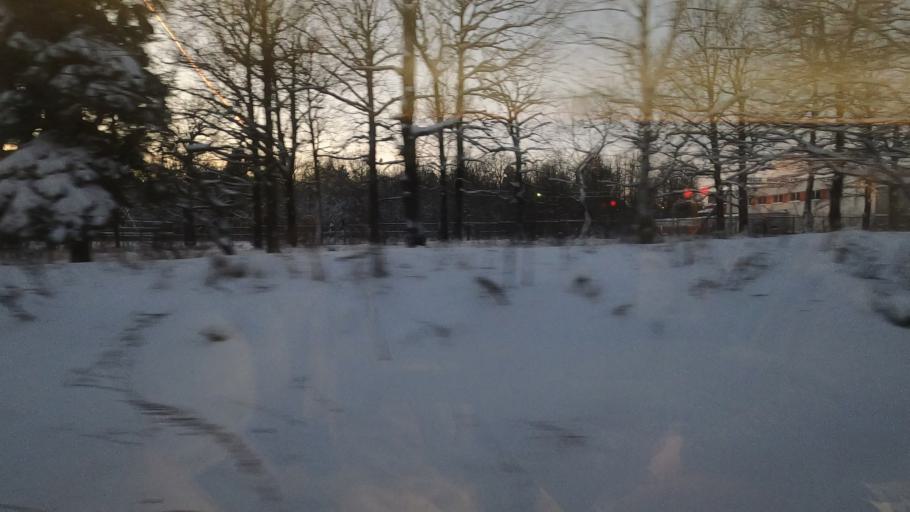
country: RU
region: Moskovskaya
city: Lugovaya
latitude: 56.0448
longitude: 37.4915
